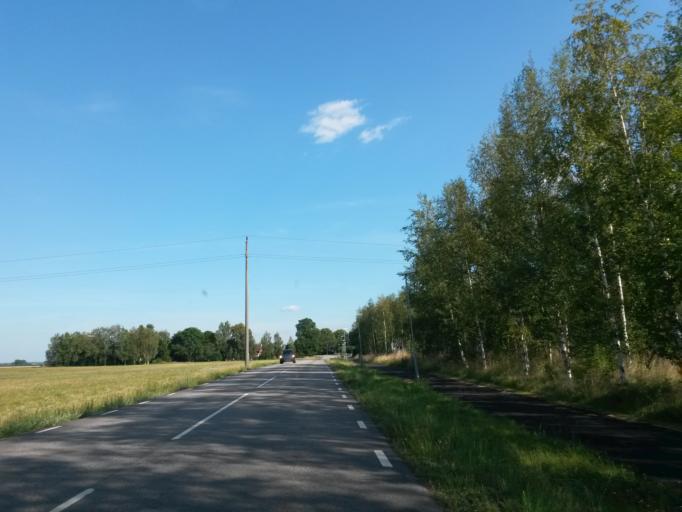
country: SE
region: Vaestra Goetaland
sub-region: Vara Kommun
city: Kvanum
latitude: 58.3327
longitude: 13.1245
